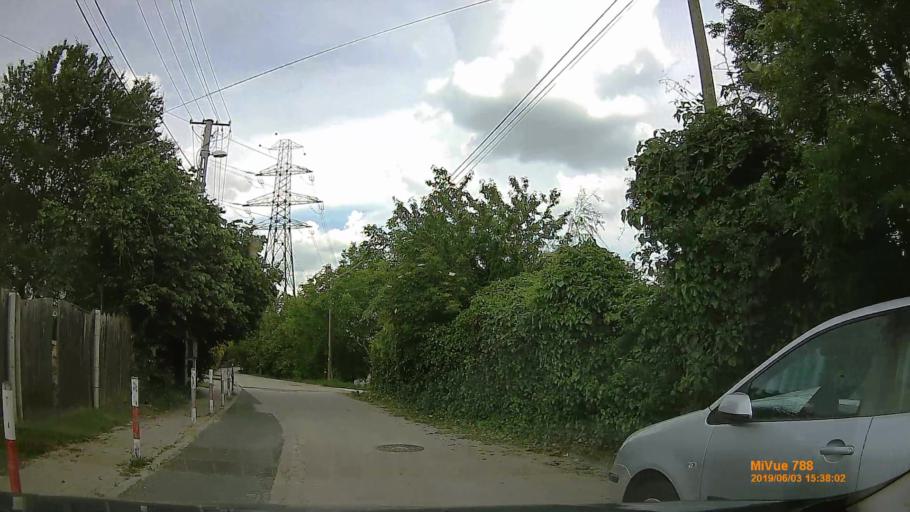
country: HU
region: Budapest
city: Budapest XXII. keruelet
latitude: 47.4321
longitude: 19.0244
